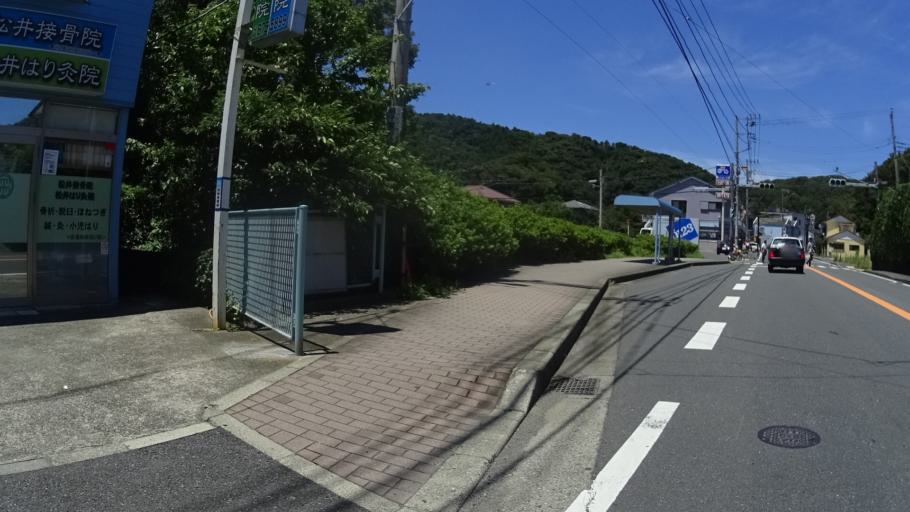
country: JP
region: Kanagawa
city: Hayama
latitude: 35.2806
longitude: 139.5798
